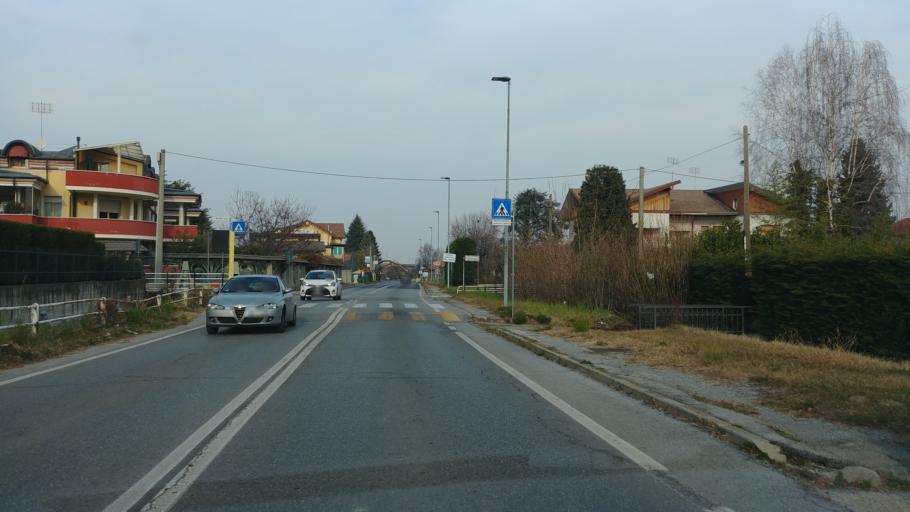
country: IT
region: Piedmont
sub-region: Provincia di Cuneo
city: Borgo San Dalmazzo
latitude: 44.3476
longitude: 7.5116
